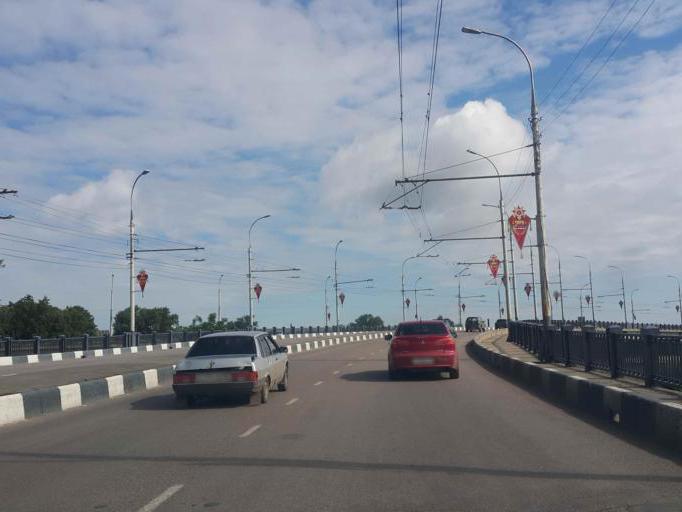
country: RU
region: Tambov
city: Tambov
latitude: 52.7209
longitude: 41.4236
